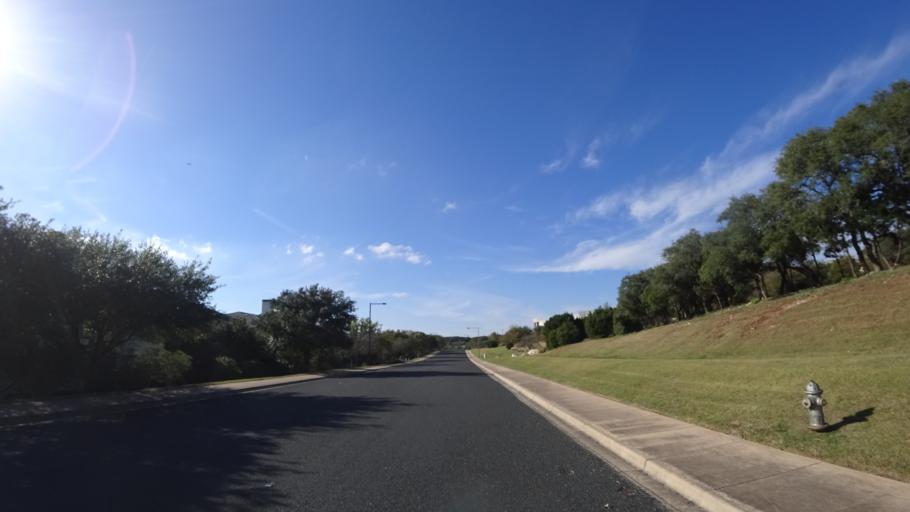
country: US
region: Texas
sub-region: Travis County
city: Barton Creek
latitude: 30.2523
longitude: -97.8706
